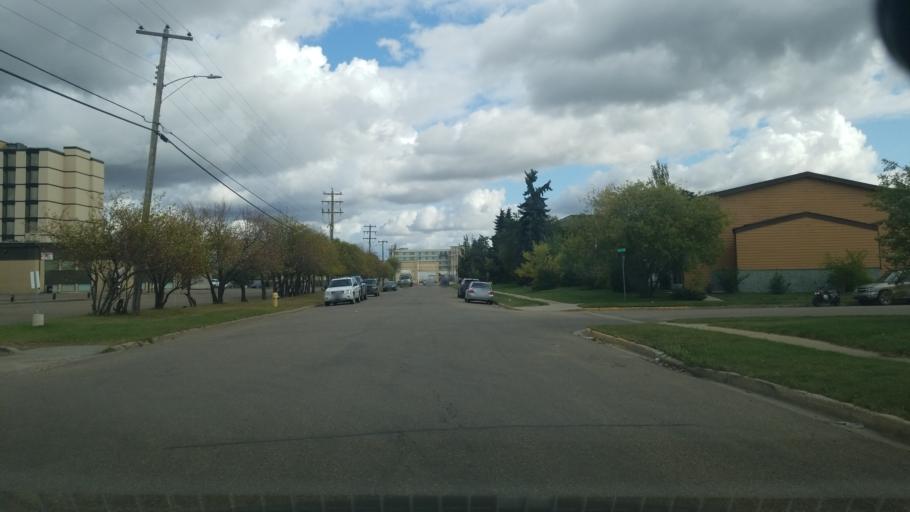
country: CA
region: Saskatchewan
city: Lloydminster
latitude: 53.2769
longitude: -110.0230
